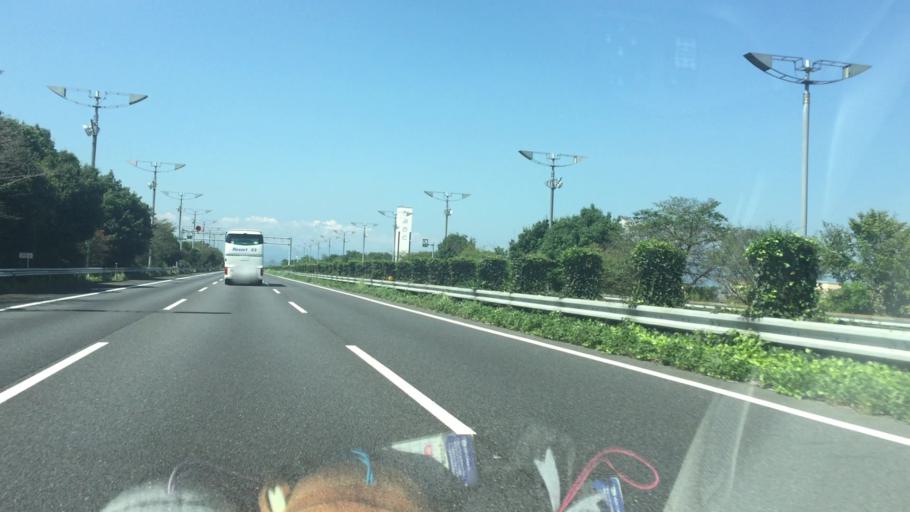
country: JP
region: Gunma
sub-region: Sawa-gun
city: Tamamura
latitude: 36.2545
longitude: 139.1217
